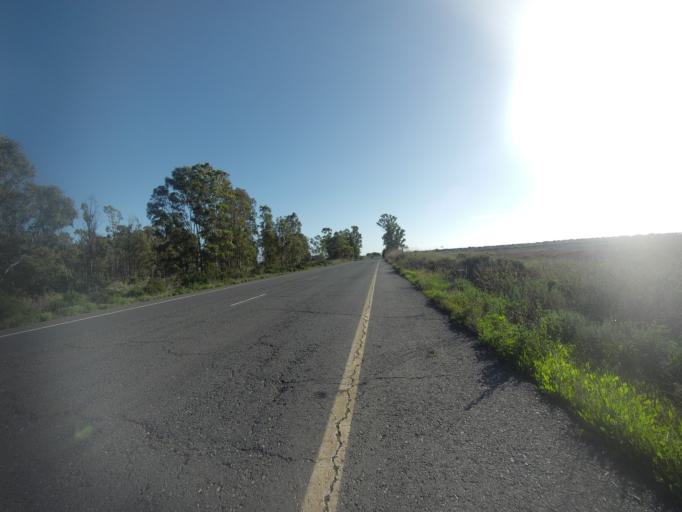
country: ES
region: Andalusia
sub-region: Provincia de Huelva
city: Huelva
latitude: 37.2391
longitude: -6.9649
